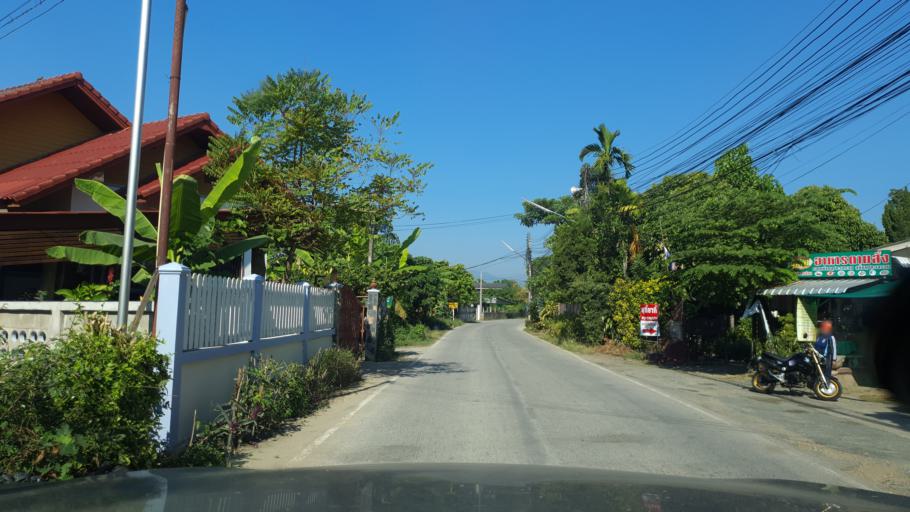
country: TH
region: Chiang Mai
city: Saraphi
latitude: 18.7351
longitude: 99.0576
